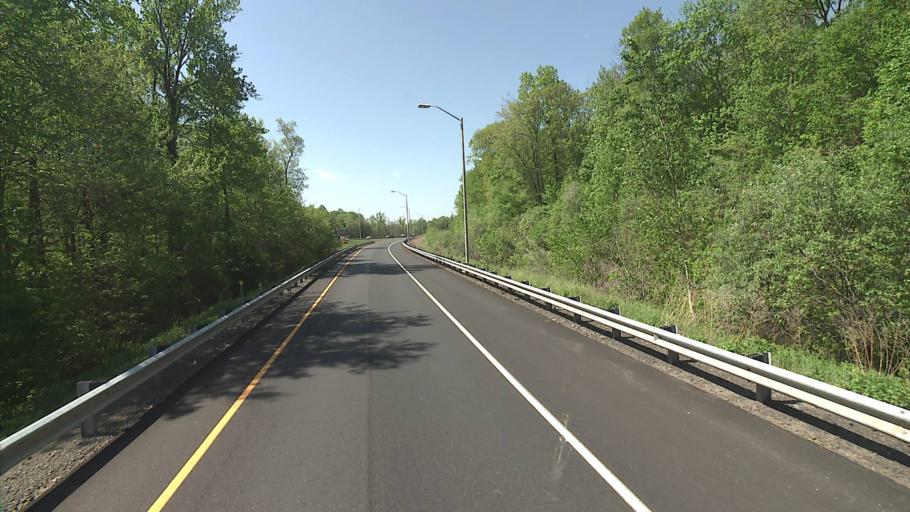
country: US
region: Connecticut
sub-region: New Haven County
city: Prospect
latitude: 41.5412
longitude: -72.9565
